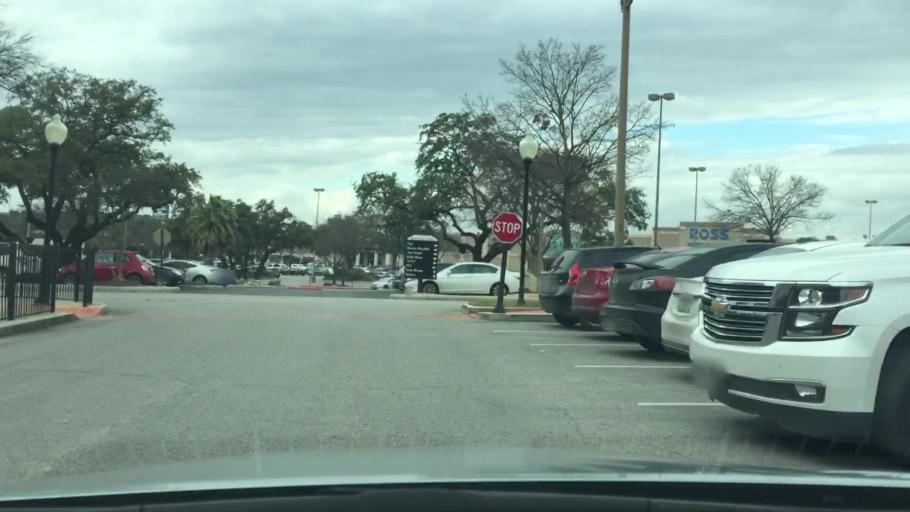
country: US
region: Texas
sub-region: Bexar County
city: Shavano Park
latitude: 29.5490
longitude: -98.5822
